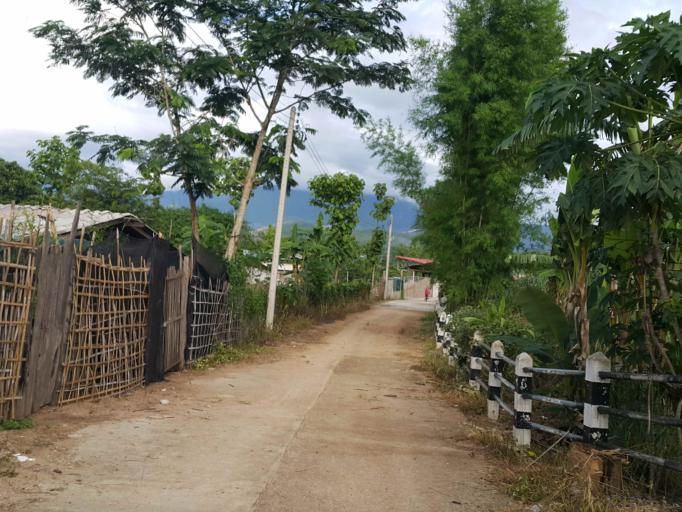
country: TH
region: Chiang Mai
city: Mae Chaem
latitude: 18.4942
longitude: 98.3625
